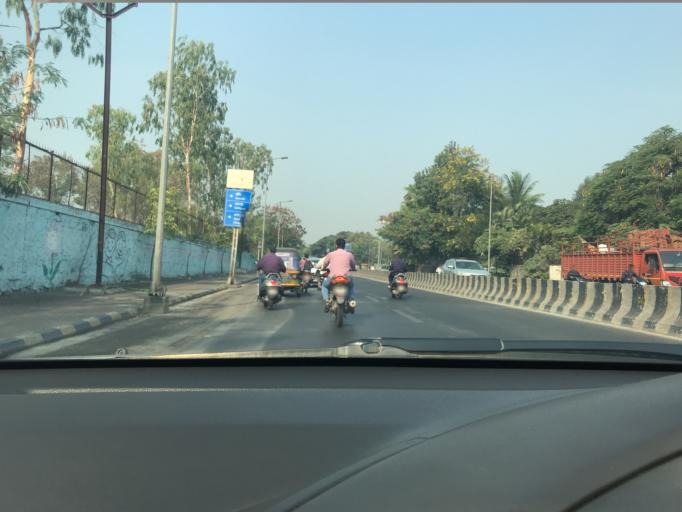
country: IN
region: Maharashtra
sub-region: Pune Division
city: Khadki
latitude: 18.5495
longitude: 73.8109
